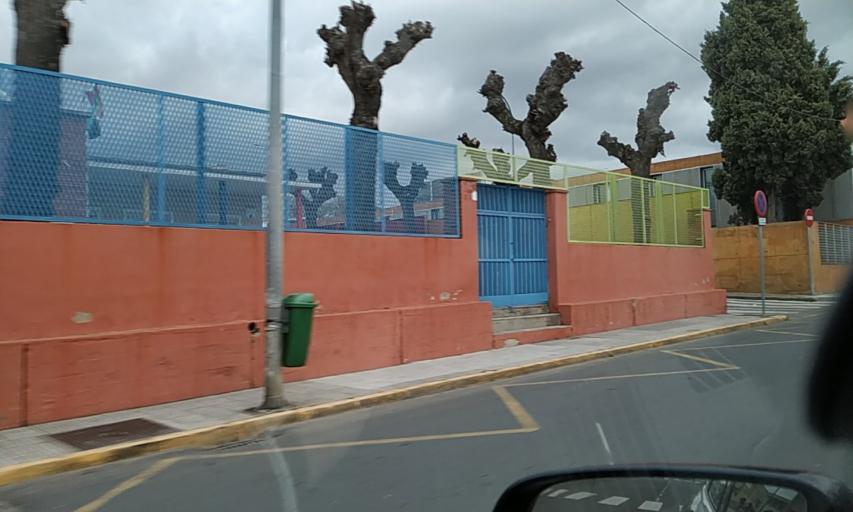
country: ES
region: Extremadura
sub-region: Provincia de Badajoz
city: Badajoz
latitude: 38.8916
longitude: -6.9789
